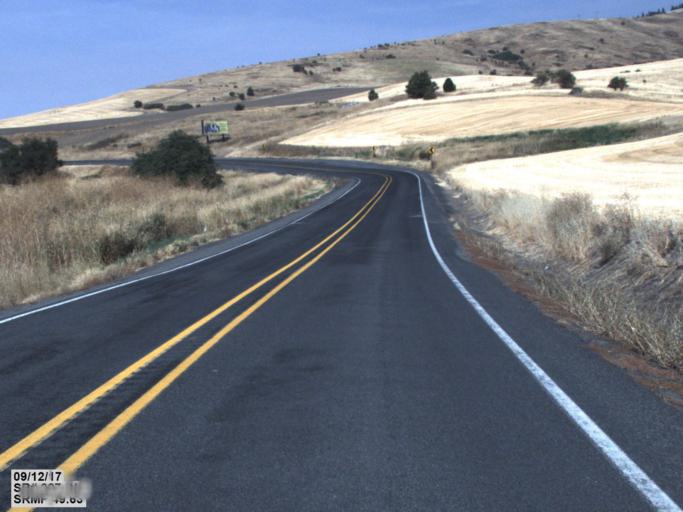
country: US
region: Idaho
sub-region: Benewah County
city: Plummer
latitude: 47.2302
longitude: -117.0948
